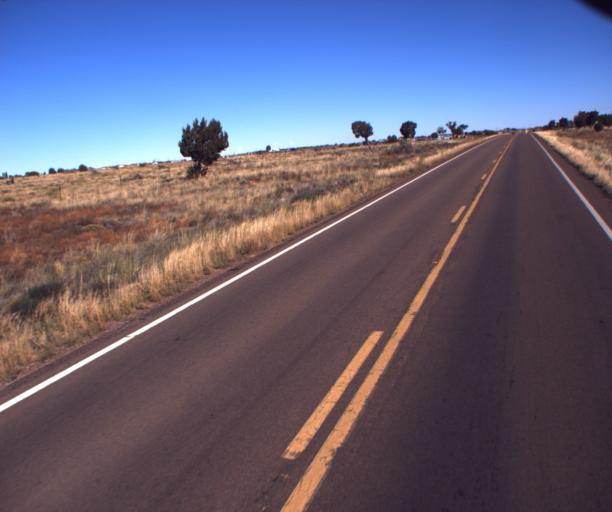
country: US
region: Arizona
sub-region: Navajo County
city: Snowflake
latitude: 34.5496
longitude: -110.0801
